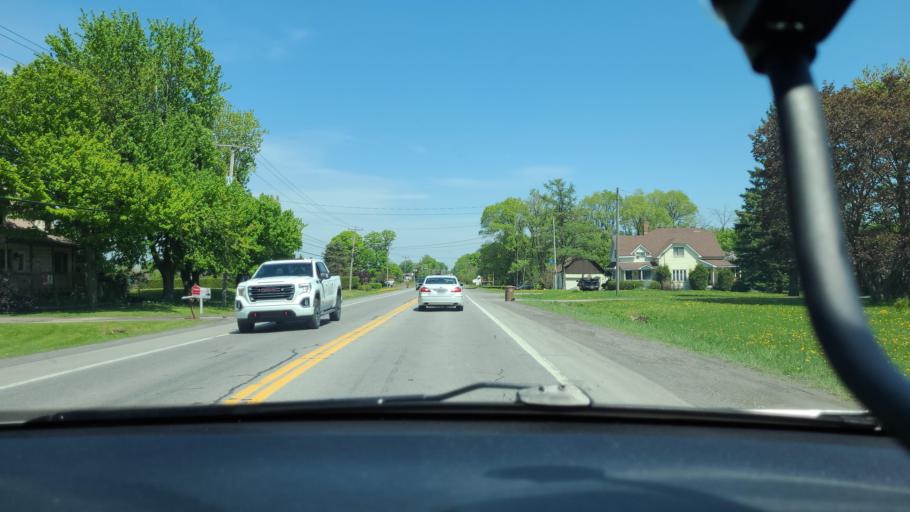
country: CA
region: Quebec
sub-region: Laurentides
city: Saint-Eustache
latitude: 45.5839
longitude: -73.9539
